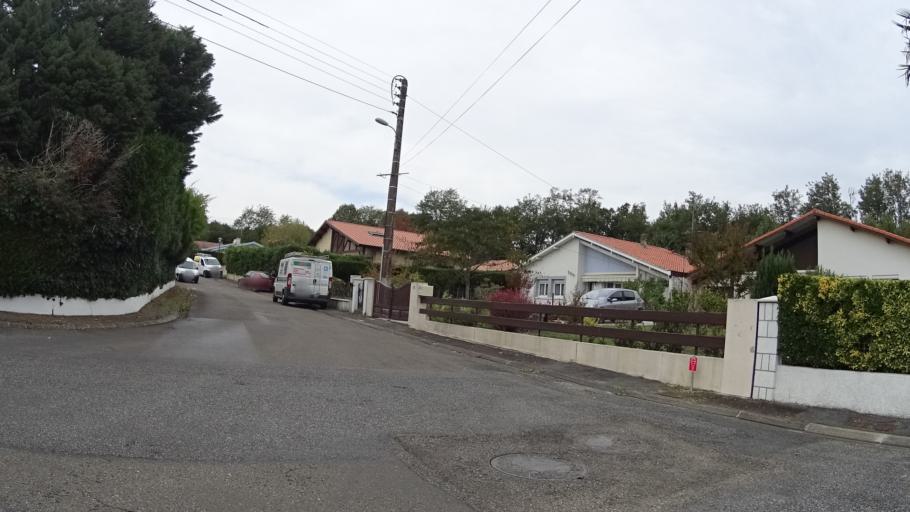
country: FR
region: Aquitaine
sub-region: Departement des Landes
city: Saint-Paul-les-Dax
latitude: 43.7309
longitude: -1.0781
